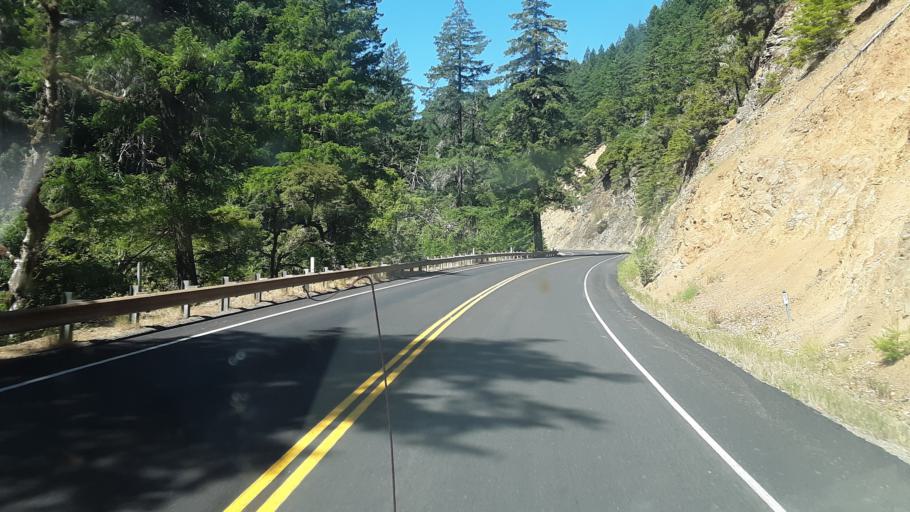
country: US
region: Oregon
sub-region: Josephine County
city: Cave Junction
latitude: 41.8975
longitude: -123.7729
